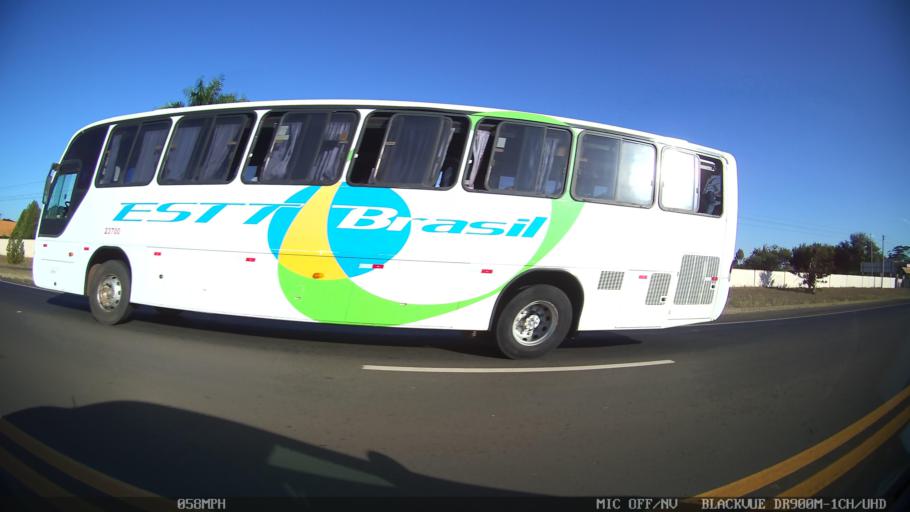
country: BR
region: Sao Paulo
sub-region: Olimpia
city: Olimpia
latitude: -20.7042
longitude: -48.9499
